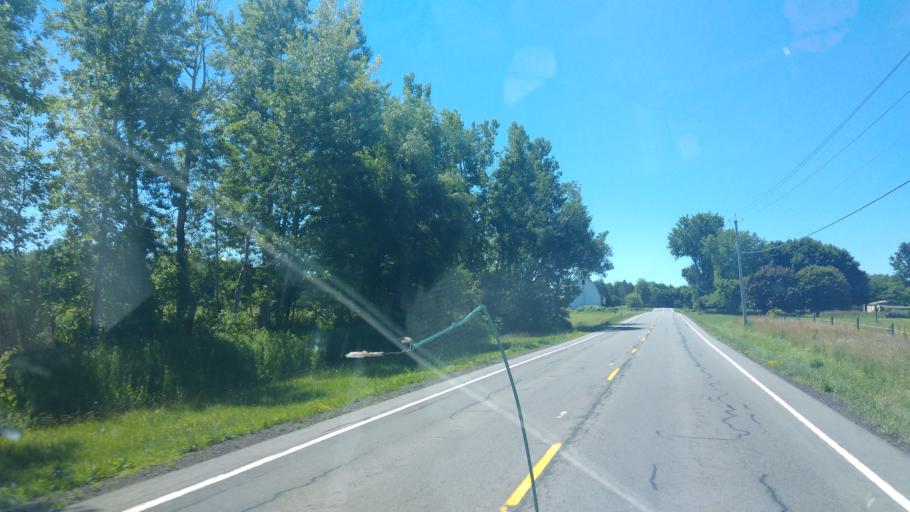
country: US
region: New York
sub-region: Wayne County
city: Sodus
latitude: 43.1973
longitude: -76.9851
